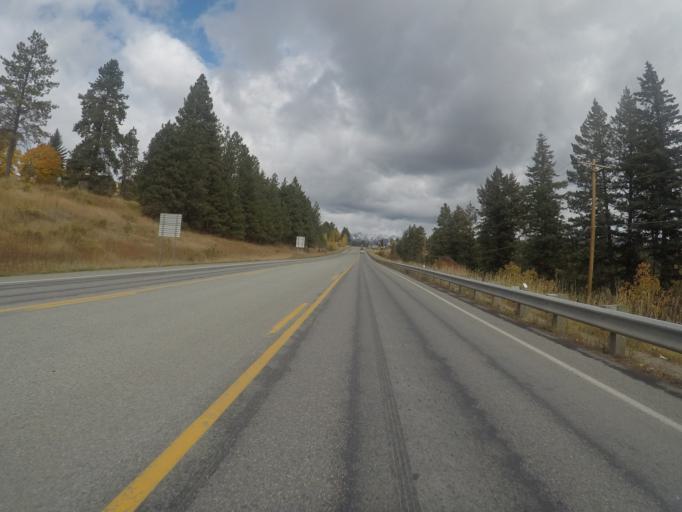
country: US
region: Montana
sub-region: Flathead County
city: Bigfork
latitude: 48.0683
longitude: -114.0809
